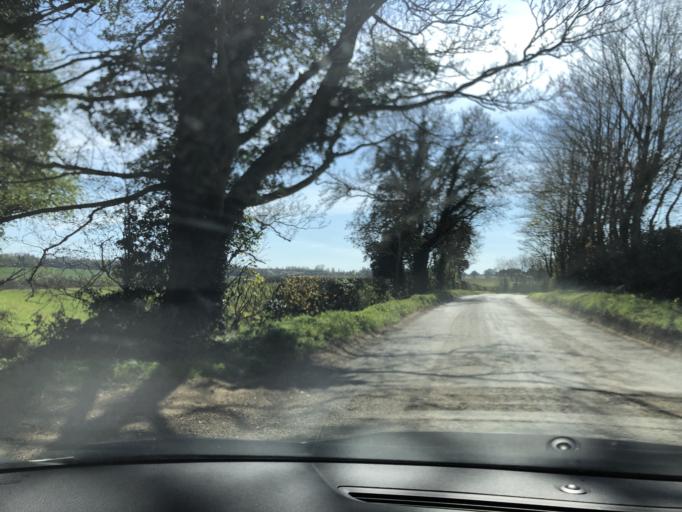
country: GB
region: England
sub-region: Oxfordshire
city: Bloxham
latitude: 52.0270
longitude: -1.4205
